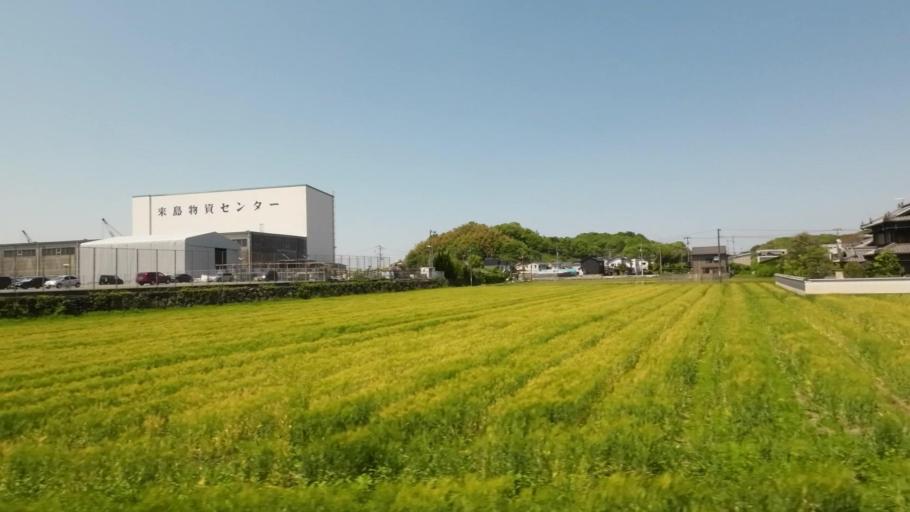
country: JP
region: Ehime
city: Hojo
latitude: 34.0743
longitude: 132.9317
